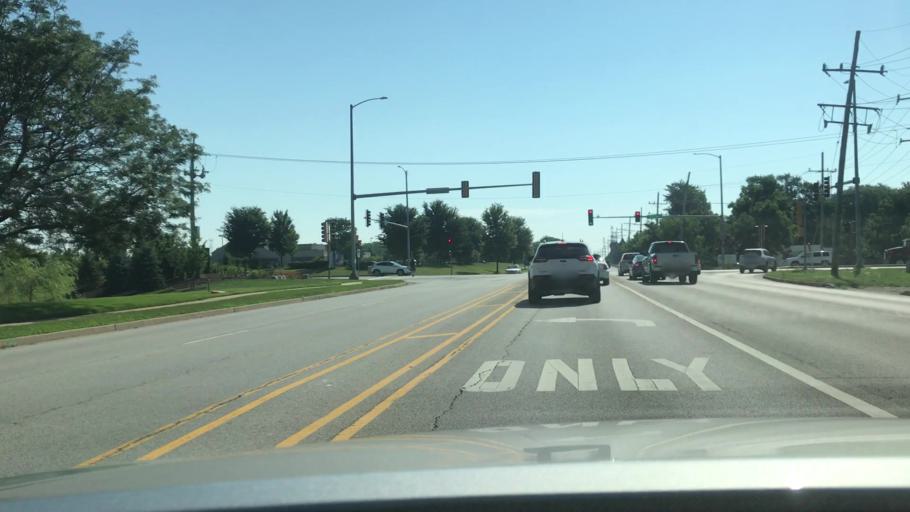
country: US
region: Illinois
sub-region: Kane County
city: Aurora
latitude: 41.7666
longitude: -88.2437
